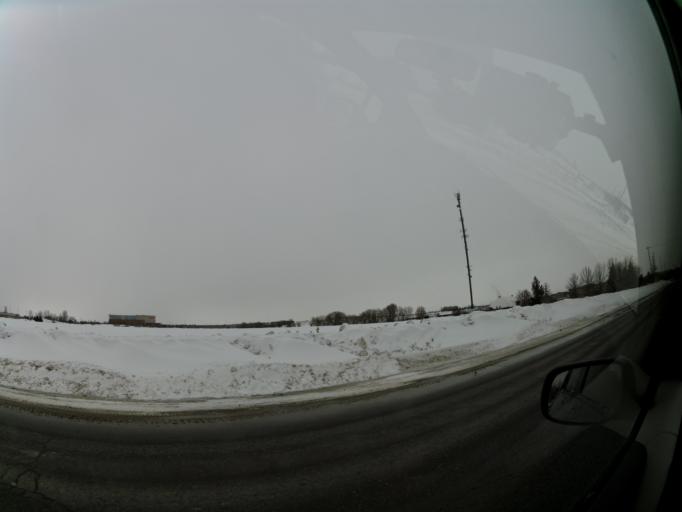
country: CA
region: Ontario
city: Bells Corners
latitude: 45.2907
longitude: -75.9179
